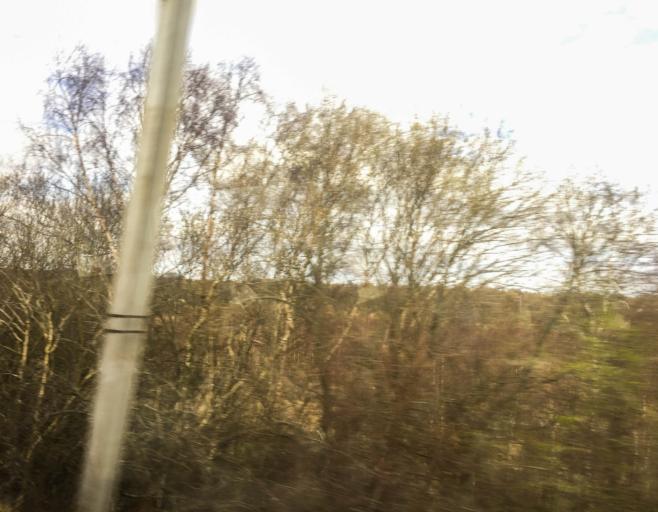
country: GB
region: Scotland
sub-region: North Lanarkshire
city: Newarthill
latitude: 55.7862
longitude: -3.9476
